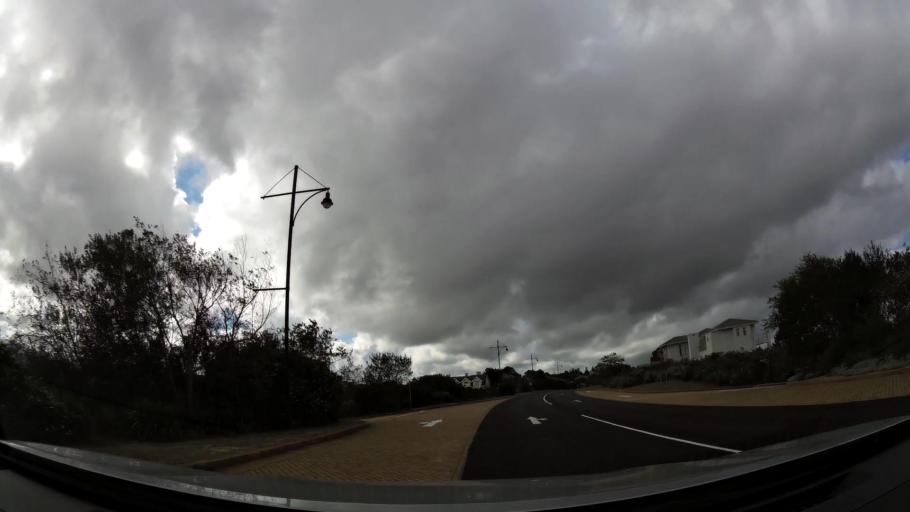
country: ZA
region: Western Cape
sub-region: Eden District Municipality
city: Knysna
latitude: -34.0676
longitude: 23.0941
